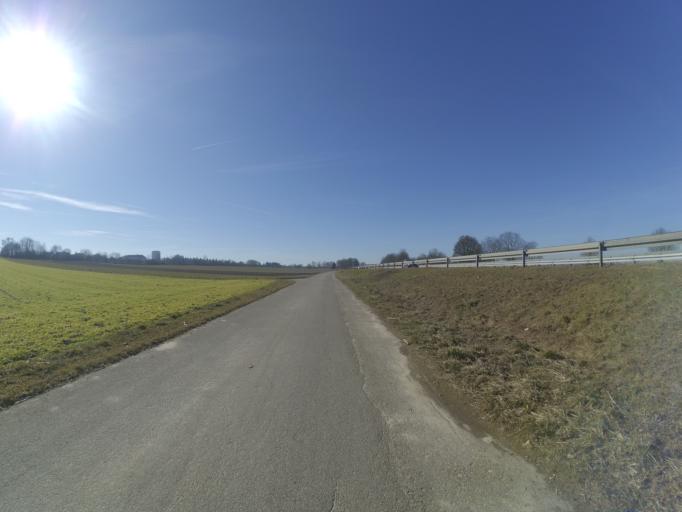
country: DE
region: Baden-Wuerttemberg
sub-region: Tuebingen Region
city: Achstetten
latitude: 48.2481
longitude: 9.8918
